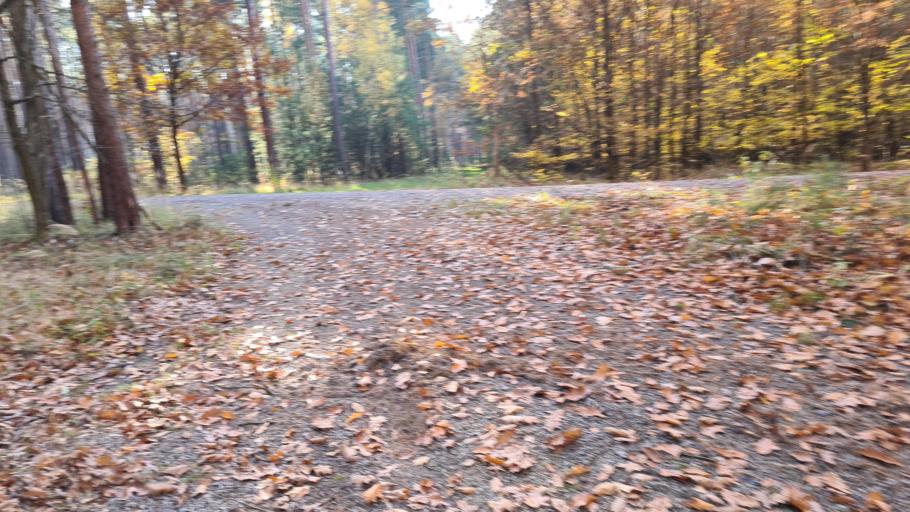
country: DE
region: Brandenburg
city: Ruckersdorf
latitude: 51.5620
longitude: 13.6230
